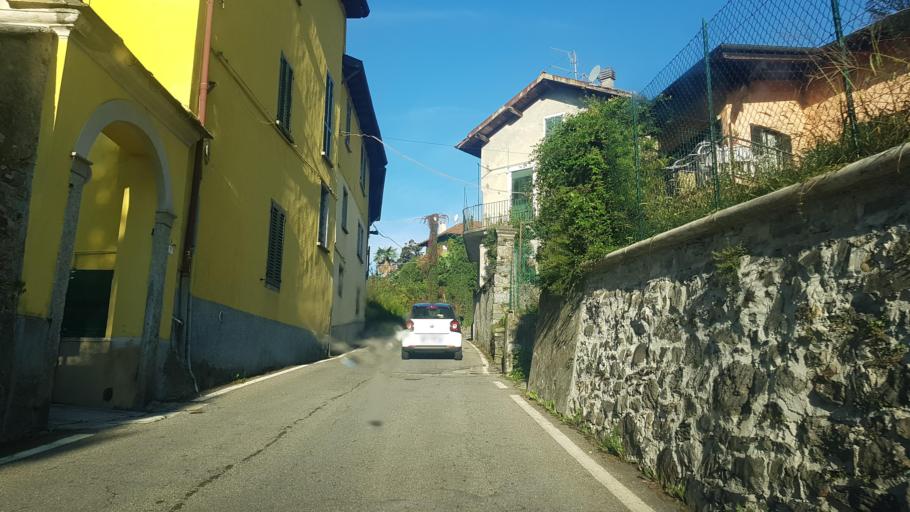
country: IT
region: Piedmont
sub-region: Provincia Verbano-Cusio-Ossola
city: Vignone
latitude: 45.9596
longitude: 8.5679
